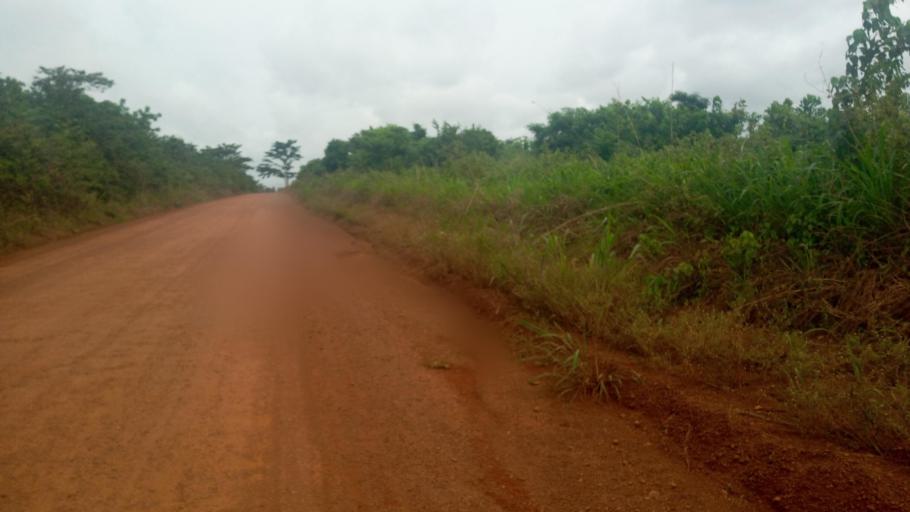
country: SL
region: Southern Province
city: Mogbwemo
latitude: 7.7398
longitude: -12.2853
